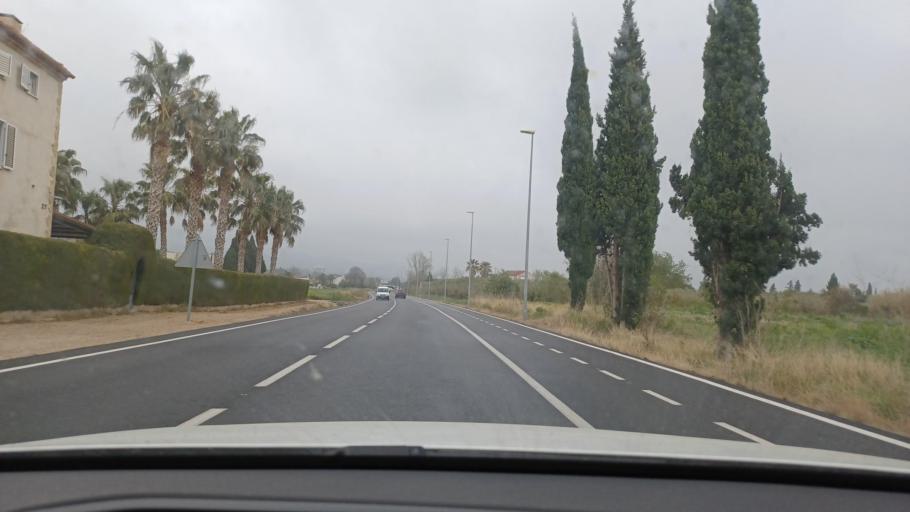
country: ES
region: Catalonia
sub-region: Provincia de Tarragona
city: Tortosa
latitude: 40.8081
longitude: 0.5010
